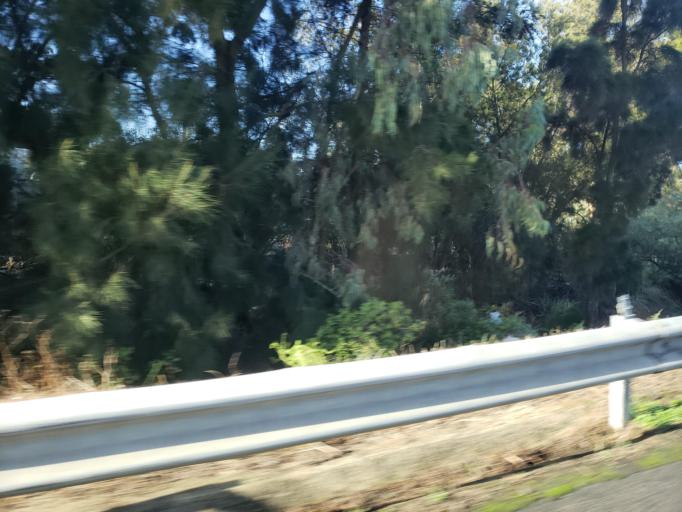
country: PT
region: Faro
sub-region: Portimao
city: Alvor
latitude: 37.1610
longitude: -8.5699
